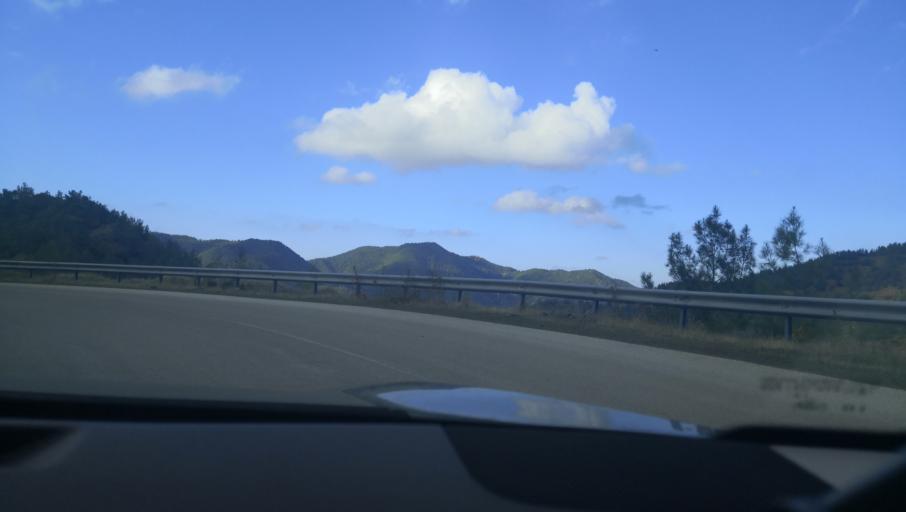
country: CY
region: Lefkosia
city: Lefka
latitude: 35.0526
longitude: 32.7450
